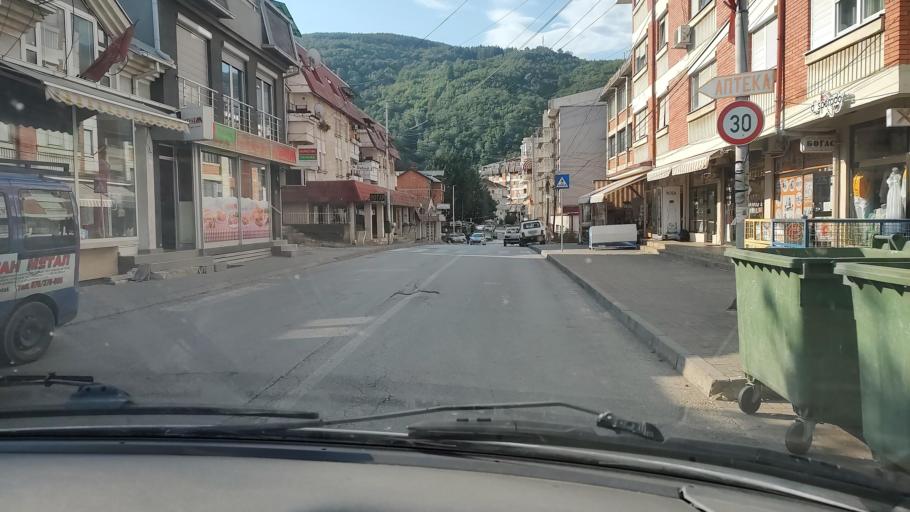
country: MK
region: Kriva Palanka
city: Kriva Palanka
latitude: 42.2039
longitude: 22.3349
